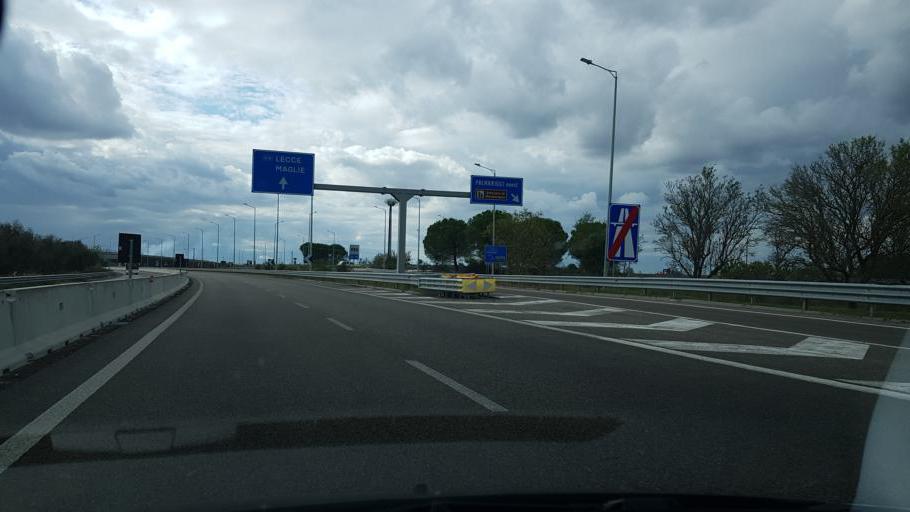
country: IT
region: Apulia
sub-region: Provincia di Lecce
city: Palmariggi
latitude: 40.1279
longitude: 18.3710
